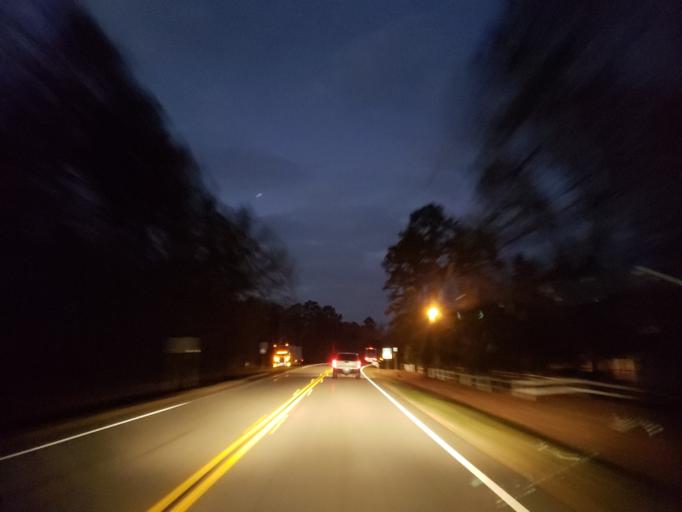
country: US
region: Georgia
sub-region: Polk County
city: Rockmart
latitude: 33.9511
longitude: -84.9995
